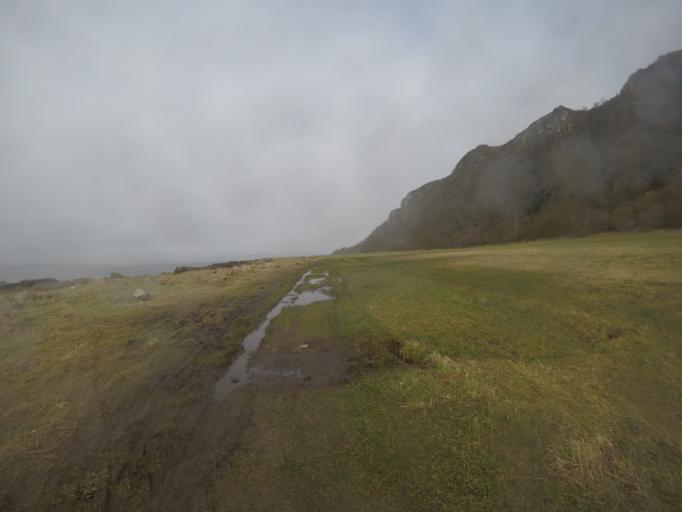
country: GB
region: Scotland
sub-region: North Ayrshire
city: Millport
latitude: 55.7071
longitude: -4.9042
